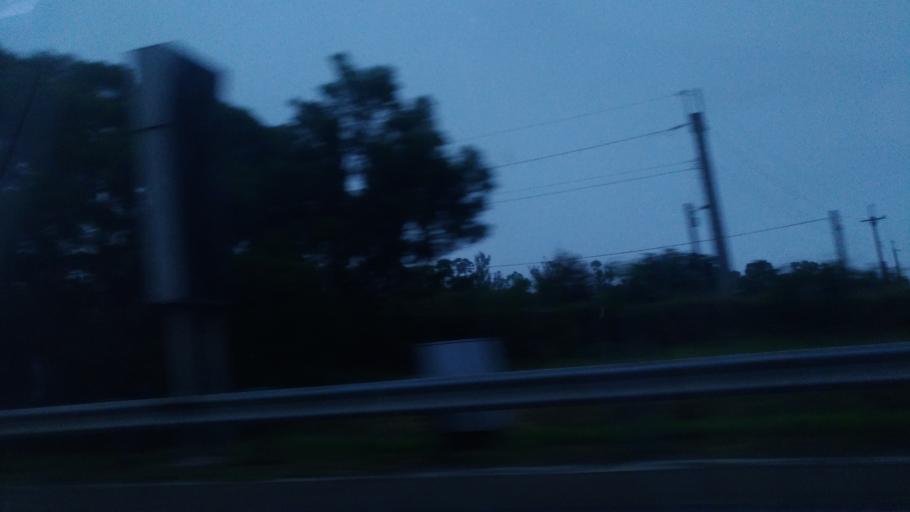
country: TW
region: Taiwan
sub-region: Hsinchu
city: Hsinchu
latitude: 24.7180
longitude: 120.8966
